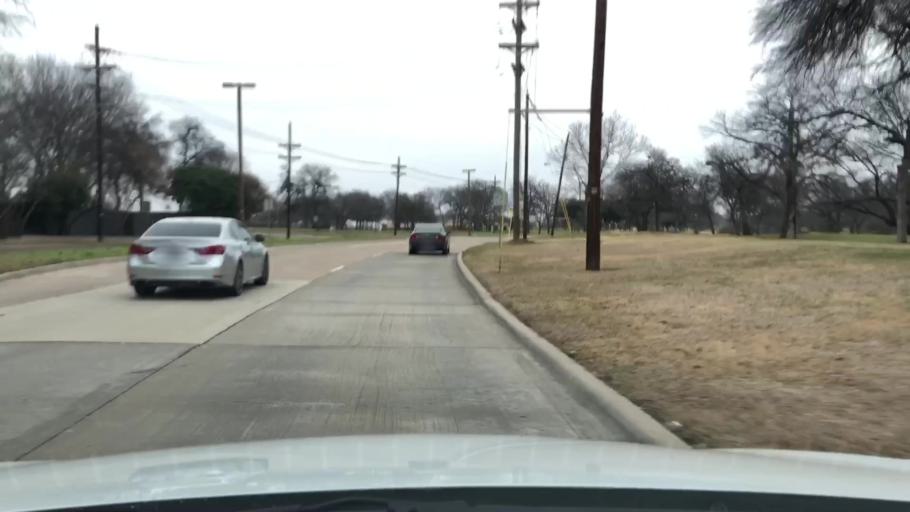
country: US
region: Texas
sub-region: Dallas County
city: Addison
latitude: 33.0184
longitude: -96.8571
